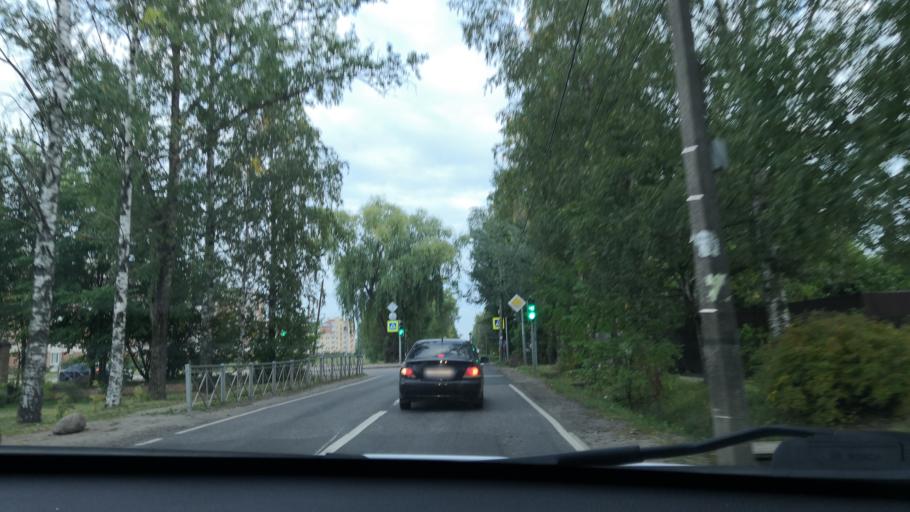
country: RU
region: St.-Petersburg
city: Pushkin
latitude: 59.6997
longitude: 30.4096
